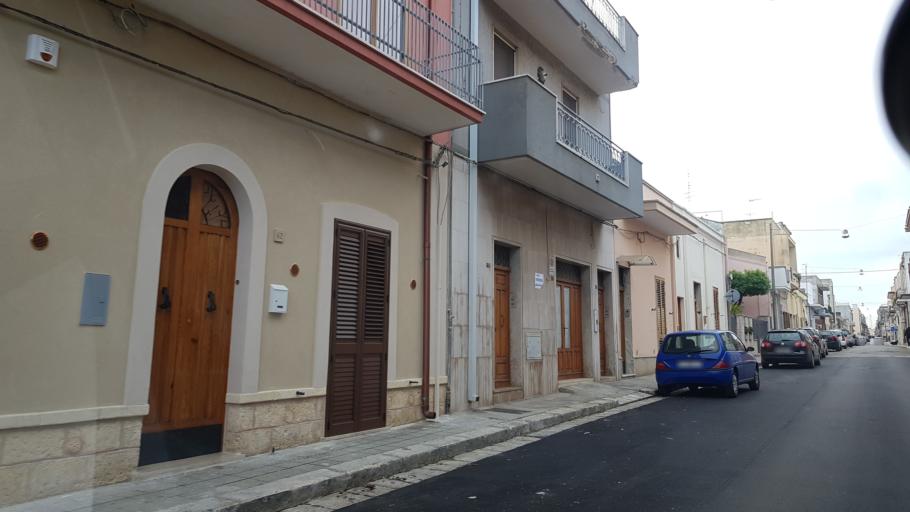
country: IT
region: Apulia
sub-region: Provincia di Brindisi
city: Mesagne
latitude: 40.5638
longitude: 17.8105
